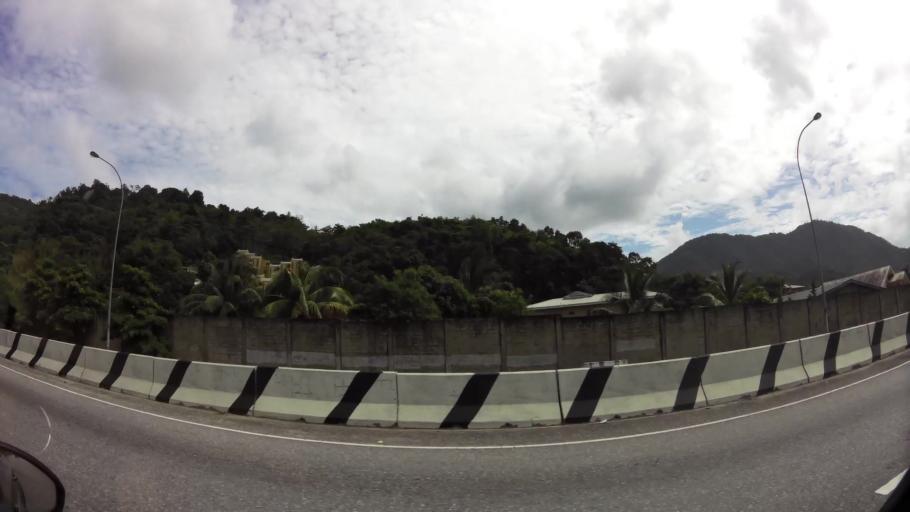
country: TT
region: Diego Martin
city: Petit Valley
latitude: 10.7160
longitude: -61.5544
